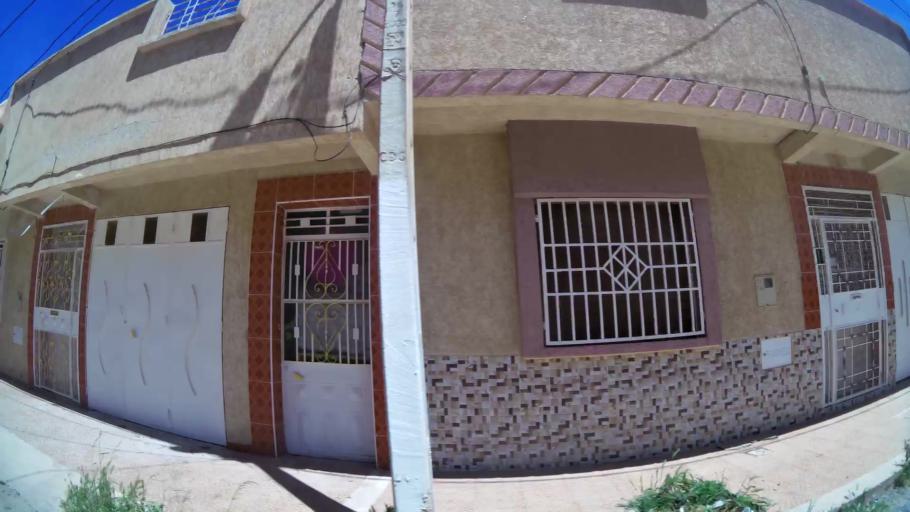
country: MA
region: Oriental
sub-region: Oujda-Angad
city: Oujda
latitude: 34.6774
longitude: -1.8543
